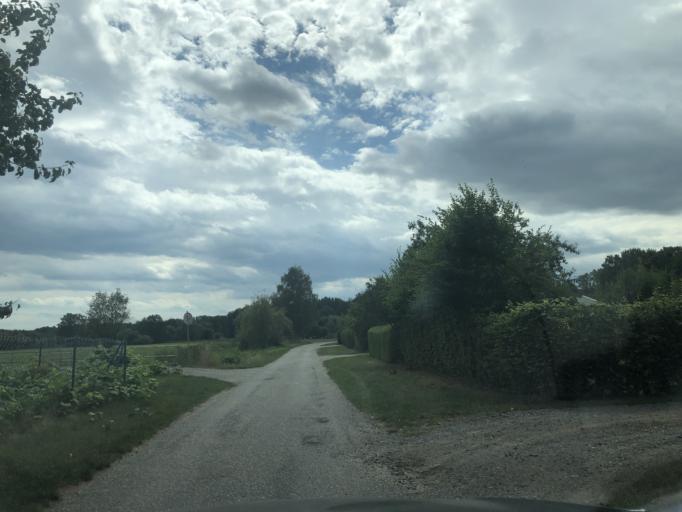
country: DE
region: Bavaria
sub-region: Upper Palatinate
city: Pressath
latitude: 49.7631
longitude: 11.9295
